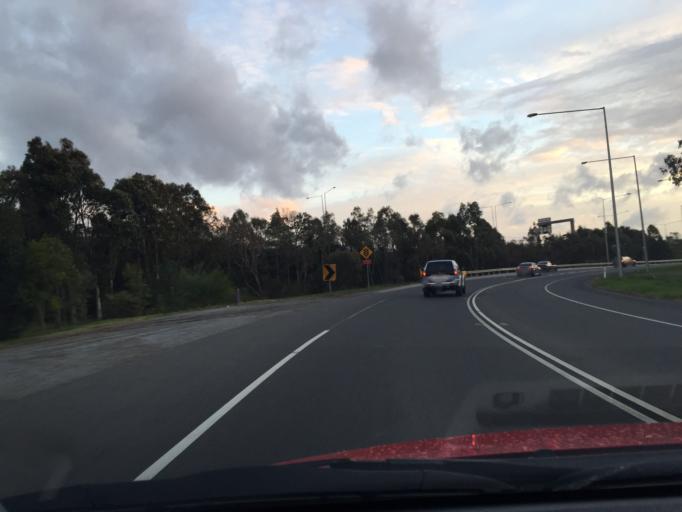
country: AU
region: Victoria
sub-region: Frankston
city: Sandhurst
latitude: -38.0693
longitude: 145.1811
